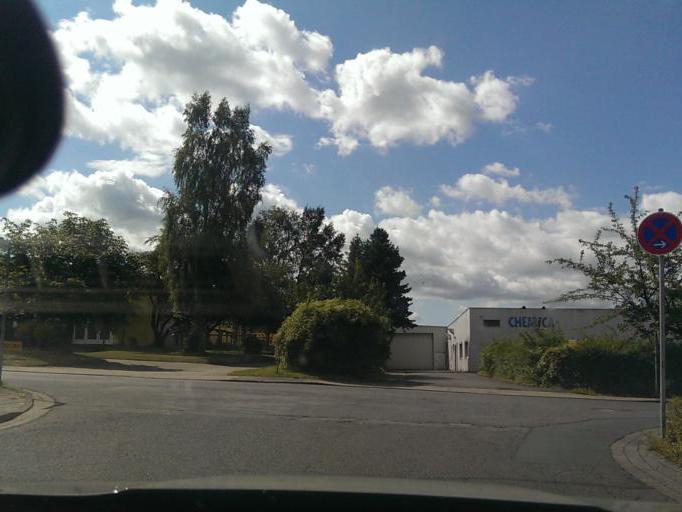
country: DE
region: Lower Saxony
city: Sarstedt
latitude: 52.2488
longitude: 9.8604
